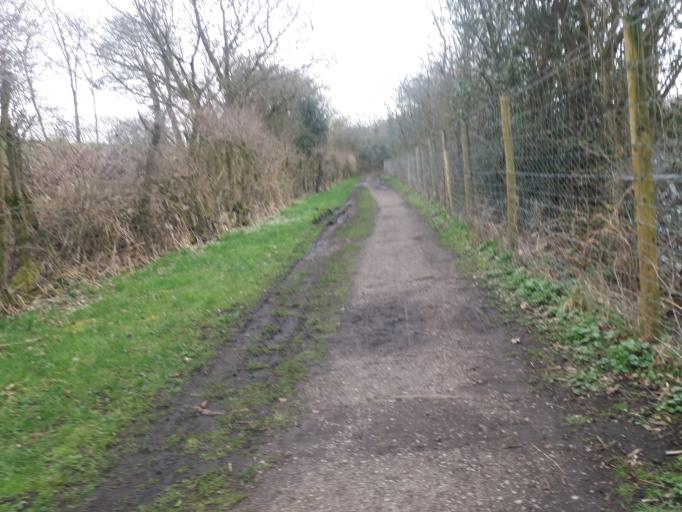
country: GB
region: England
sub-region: Lancashire
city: Chorley
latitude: 53.6586
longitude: -2.6083
